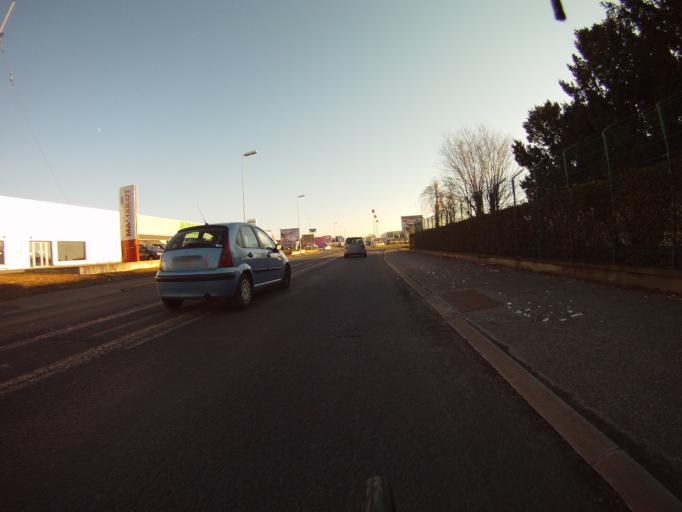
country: FR
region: Auvergne
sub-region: Departement du Puy-de-Dome
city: Perignat-les-Sarlieve
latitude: 45.7515
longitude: 3.1583
